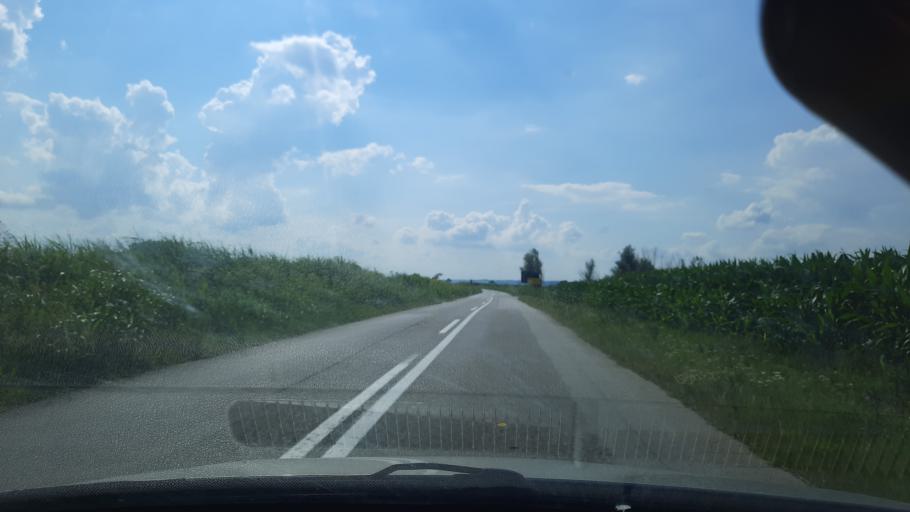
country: RS
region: Central Serbia
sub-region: Branicevski Okrug
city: Malo Crnice
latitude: 44.5802
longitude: 21.3227
